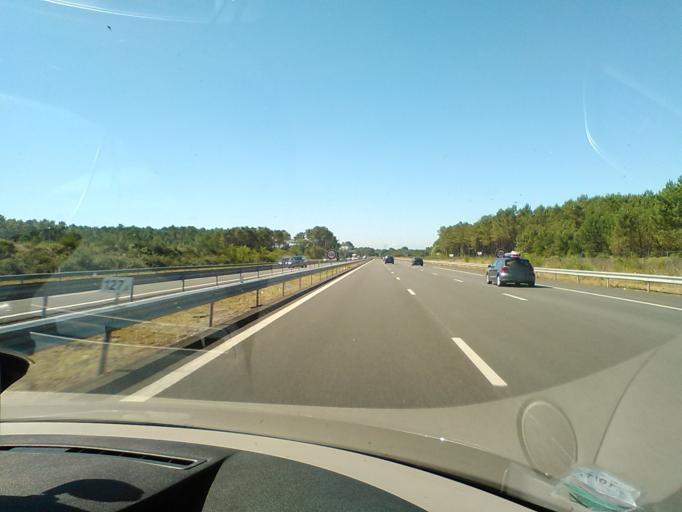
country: FR
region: Aquitaine
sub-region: Departement des Landes
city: Magescq
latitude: 43.8012
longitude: -1.2033
